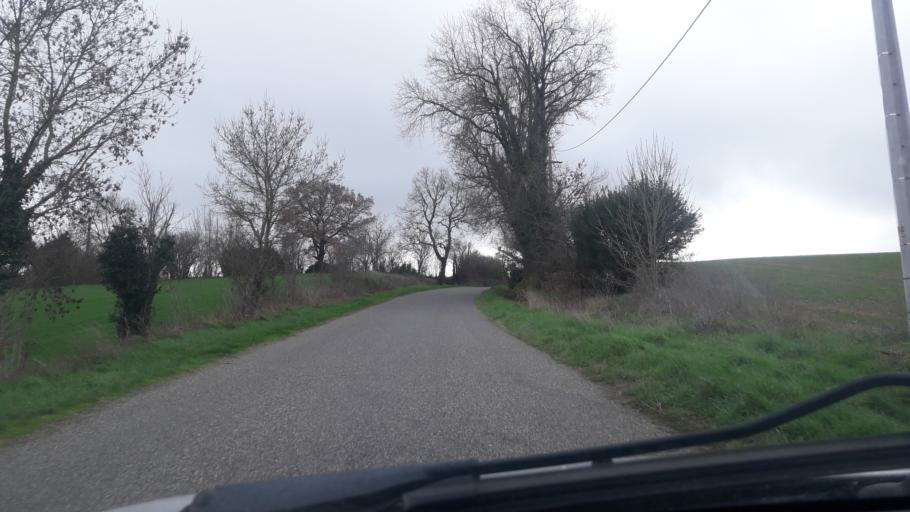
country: FR
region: Midi-Pyrenees
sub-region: Departement du Gers
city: Gimont
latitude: 43.6513
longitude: 1.0063
